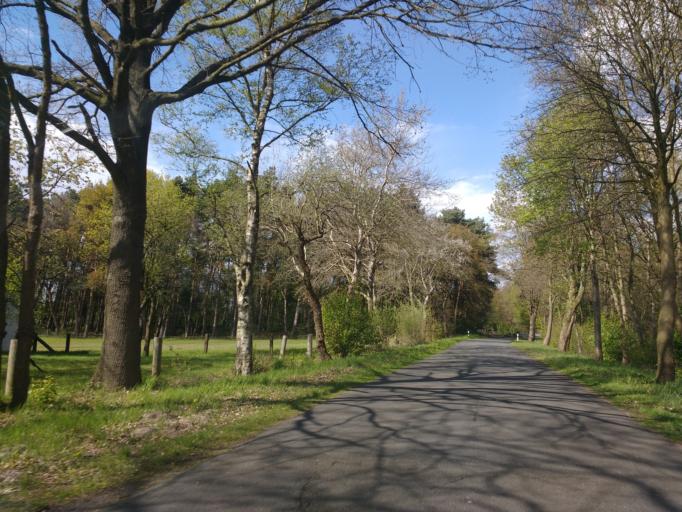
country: DE
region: North Rhine-Westphalia
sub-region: Regierungsbezirk Detmold
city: Hovelhof
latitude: 51.7784
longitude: 8.6667
